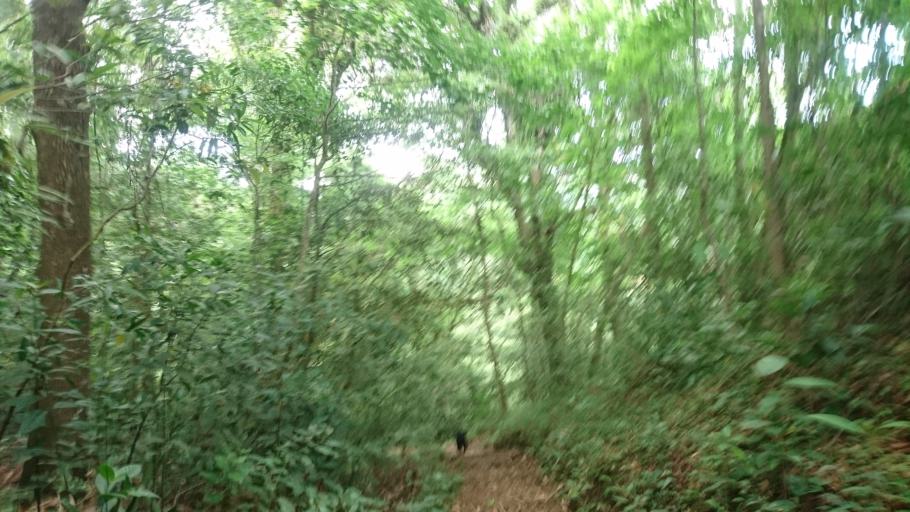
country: GT
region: Huehuetenango
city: Union
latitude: 16.1326
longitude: -91.7273
